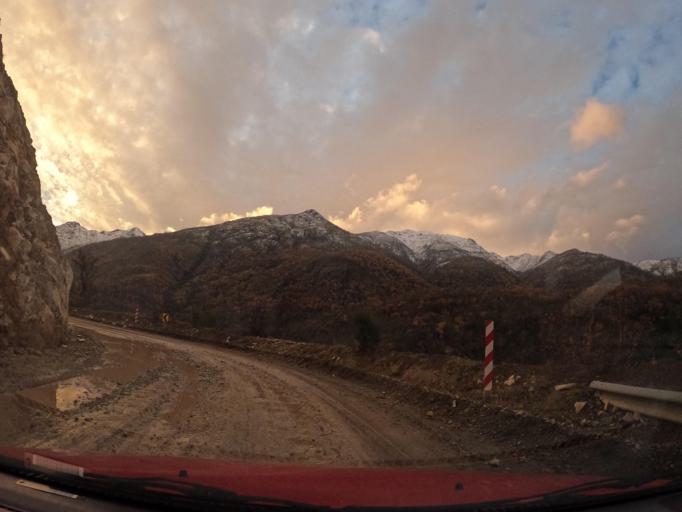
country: CL
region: Maule
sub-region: Provincia de Linares
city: Colbun
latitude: -35.8573
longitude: -71.1630
